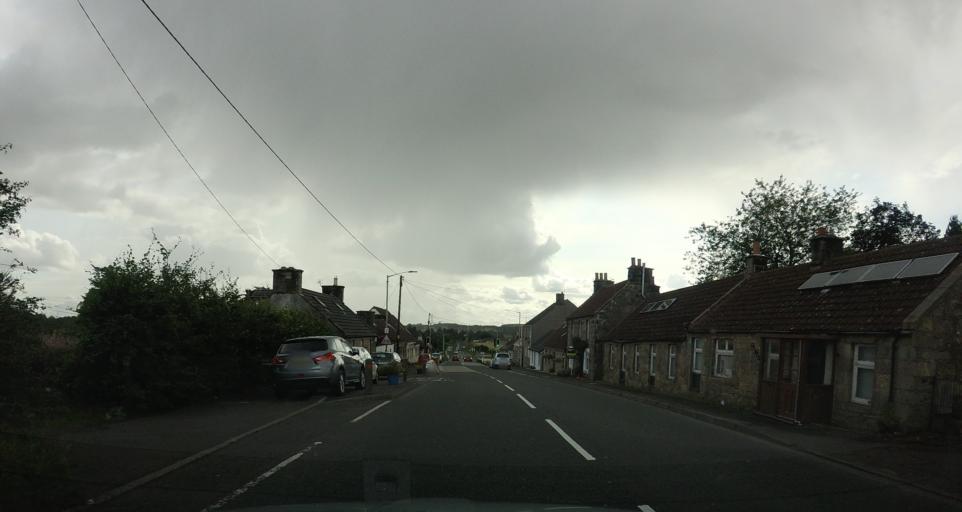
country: GB
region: Scotland
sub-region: Clackmannanshire
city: Dollar
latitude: 56.1537
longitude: -3.6338
